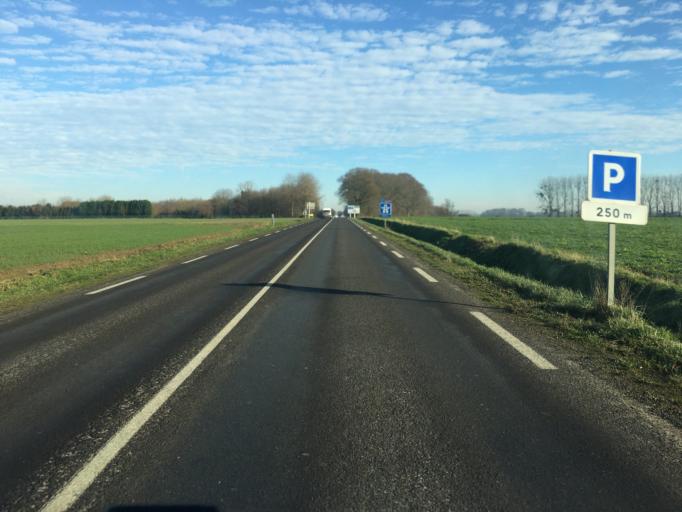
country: FR
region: Haute-Normandie
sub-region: Departement de la Seine-Maritime
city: Sainte-Marie-des-Champs
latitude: 49.6428
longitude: 0.8354
